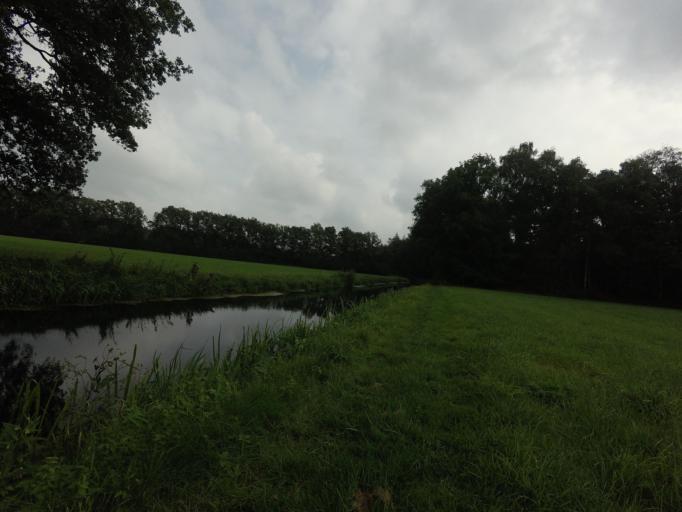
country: NL
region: Gelderland
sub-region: Gemeente Lochem
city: Harfsen
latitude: 52.2839
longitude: 6.2799
